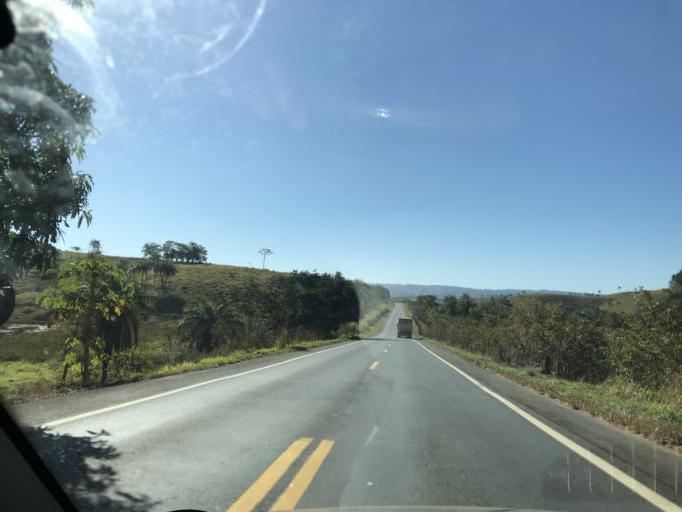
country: BR
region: Minas Gerais
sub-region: Bambui
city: Bambui
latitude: -19.8638
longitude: -45.9857
